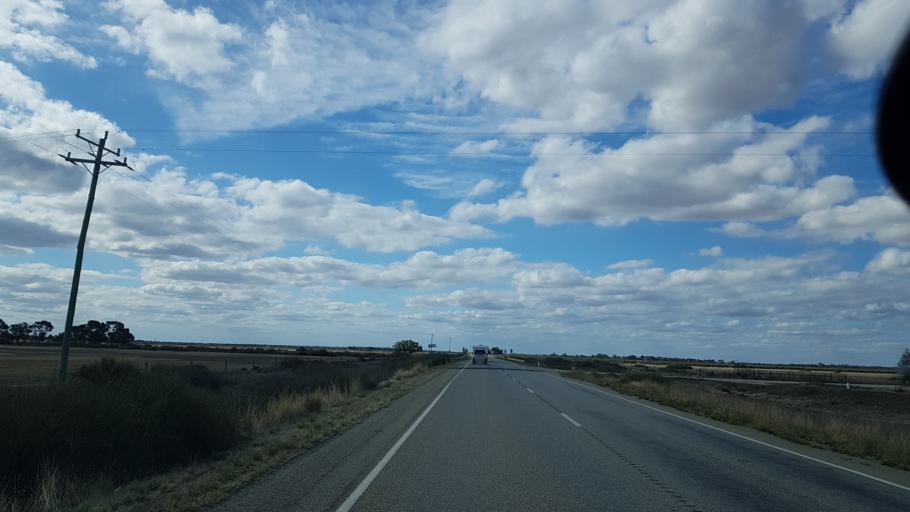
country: AU
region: Victoria
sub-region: Swan Hill
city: Swan Hill
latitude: -35.8572
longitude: 143.9358
